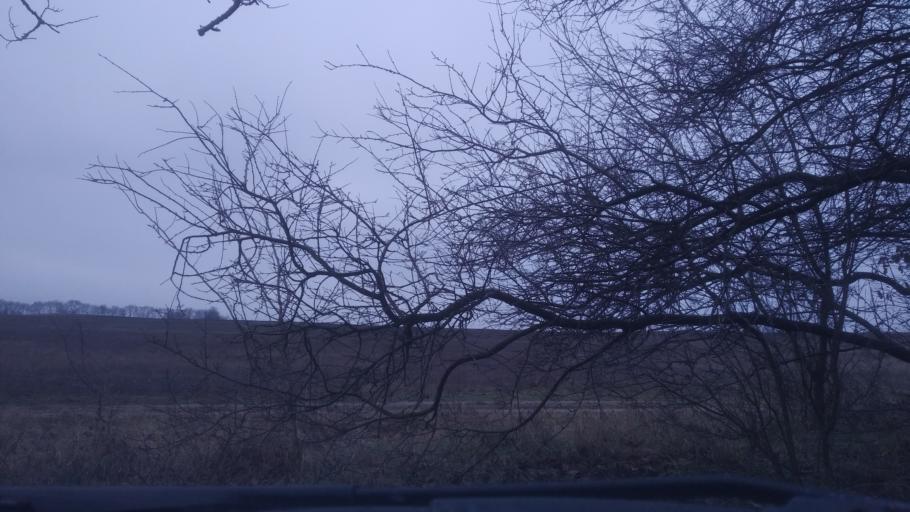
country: HU
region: Komarom-Esztergom
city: Dunaalmas
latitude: 47.7079
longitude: 18.3111
